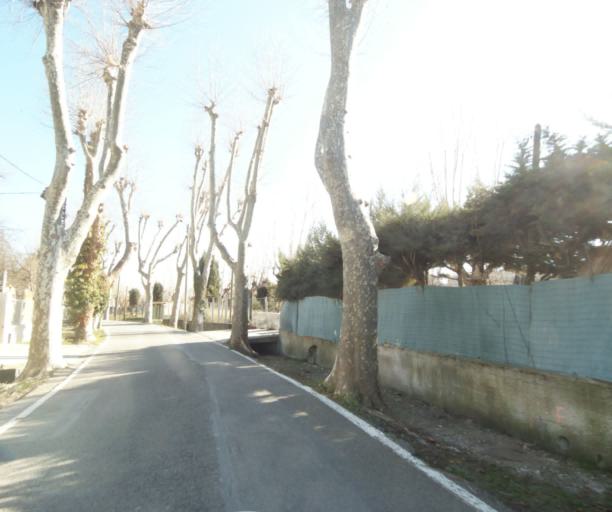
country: FR
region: Provence-Alpes-Cote d'Azur
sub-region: Departement des Alpes-Maritimes
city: Biot
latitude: 43.6129
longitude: 7.1186
